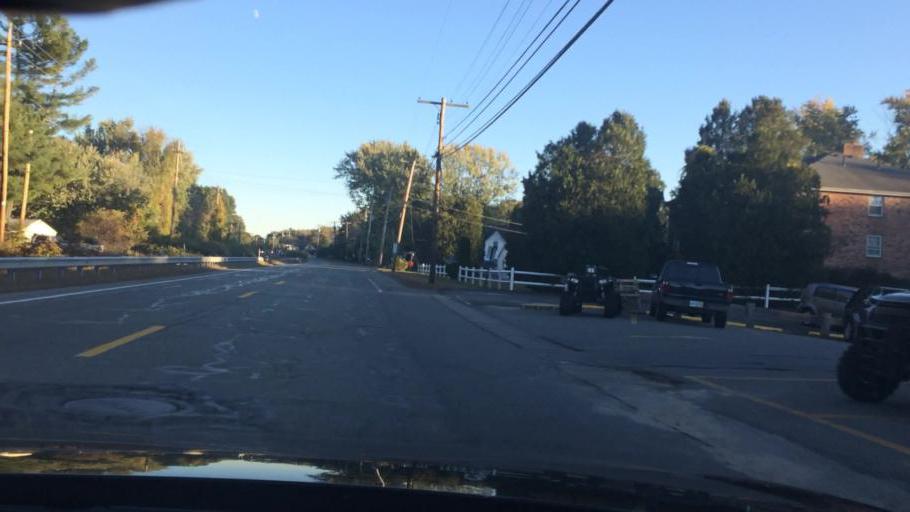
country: US
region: Massachusetts
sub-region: Middlesex County
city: Tyngsboro
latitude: 42.6483
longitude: -71.3970
